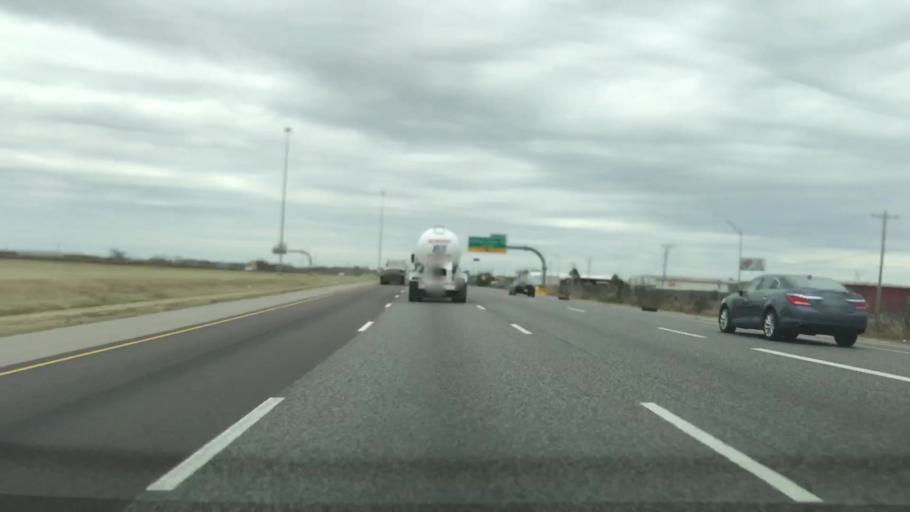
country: US
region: Oklahoma
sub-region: Cleveland County
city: Moore
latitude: 35.2831
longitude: -97.4845
